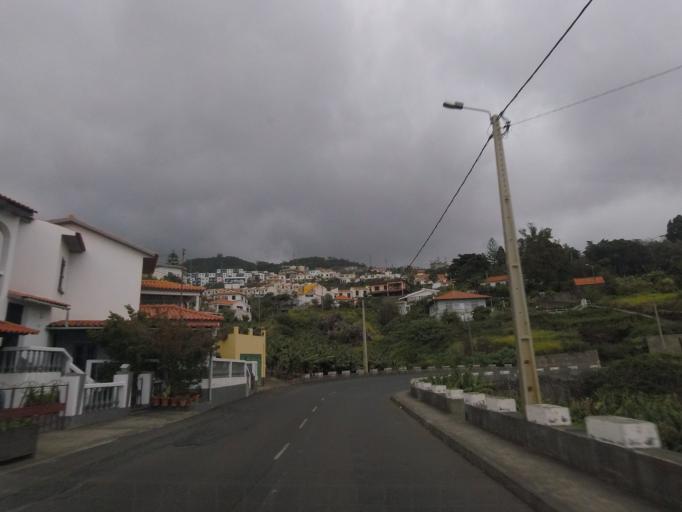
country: PT
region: Madeira
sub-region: Machico
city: Machico
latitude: 32.7074
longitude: -16.7673
